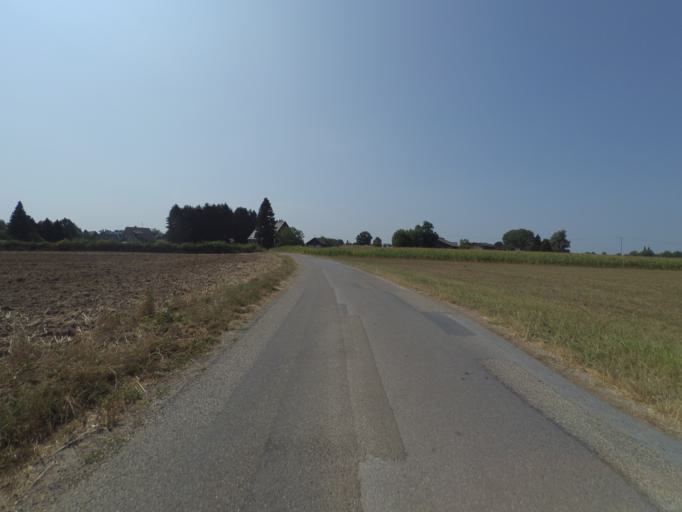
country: DE
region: North Rhine-Westphalia
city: Rees
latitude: 51.8169
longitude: 6.4079
